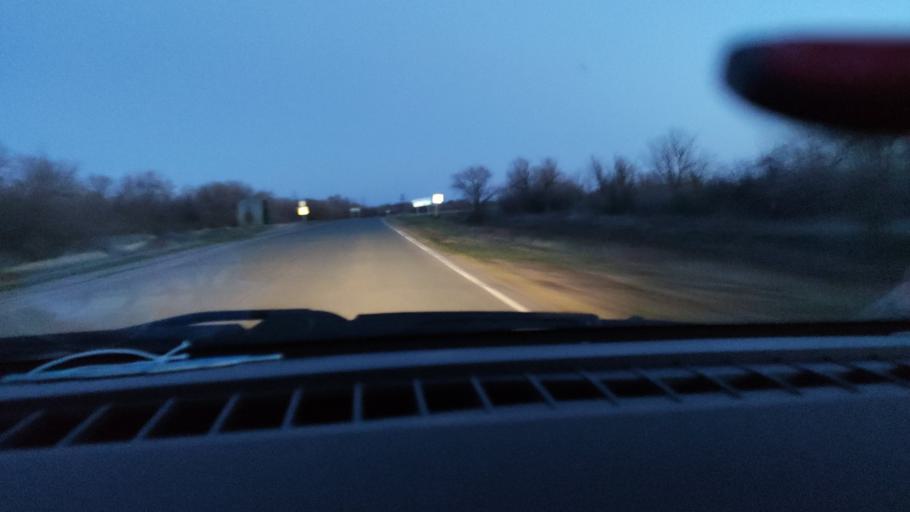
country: RU
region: Saratov
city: Rovnoye
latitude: 50.9428
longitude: 46.1273
